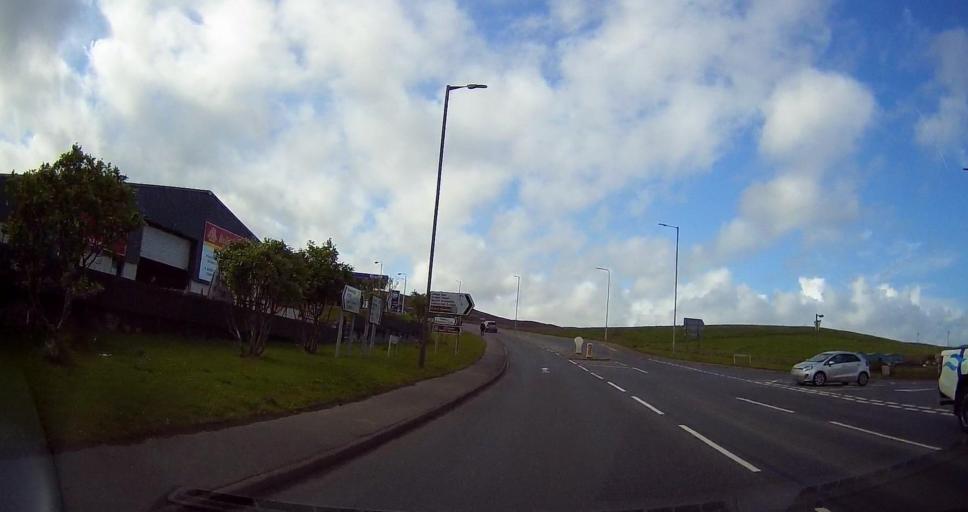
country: GB
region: Scotland
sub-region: Shetland Islands
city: Lerwick
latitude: 60.1684
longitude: -1.1662
